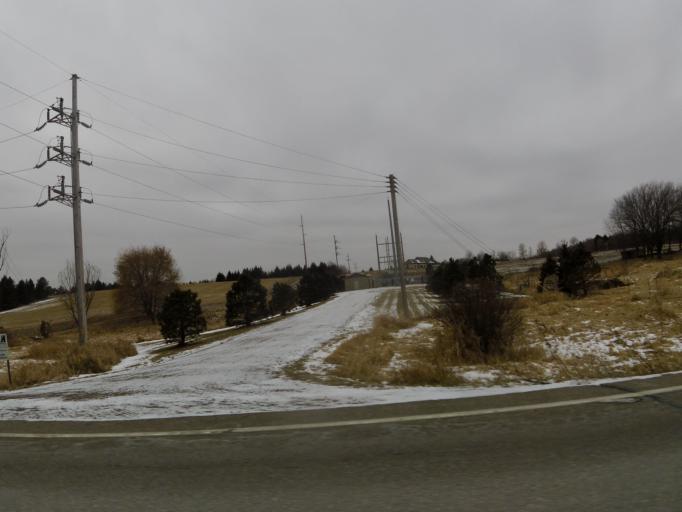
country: US
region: Minnesota
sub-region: Hennepin County
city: Independence
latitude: 45.0215
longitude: -93.7273
